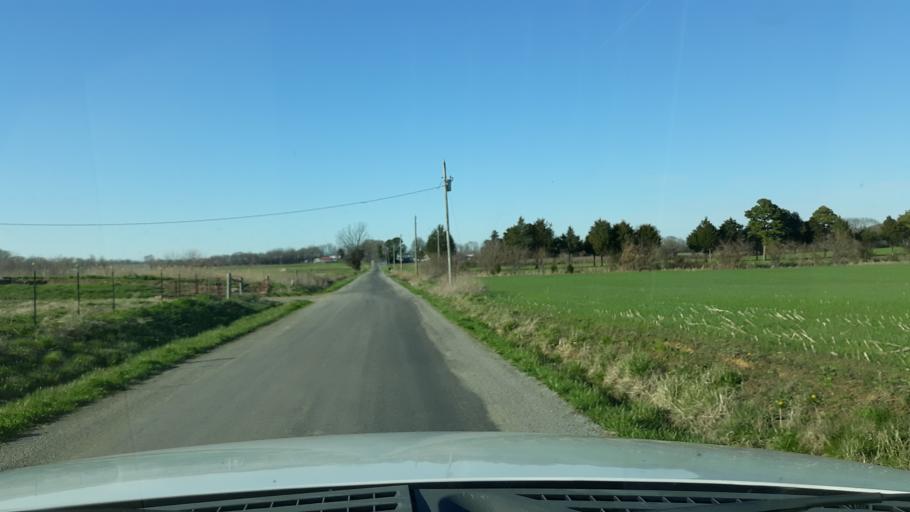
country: US
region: Illinois
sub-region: Saline County
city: Harrisburg
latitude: 37.7990
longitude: -88.6055
